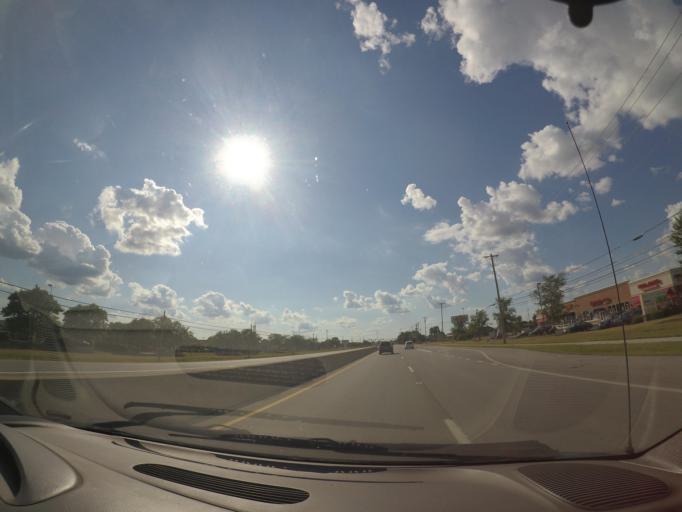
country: US
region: Ohio
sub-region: Wood County
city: Perrysburg
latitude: 41.5441
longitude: -83.5883
